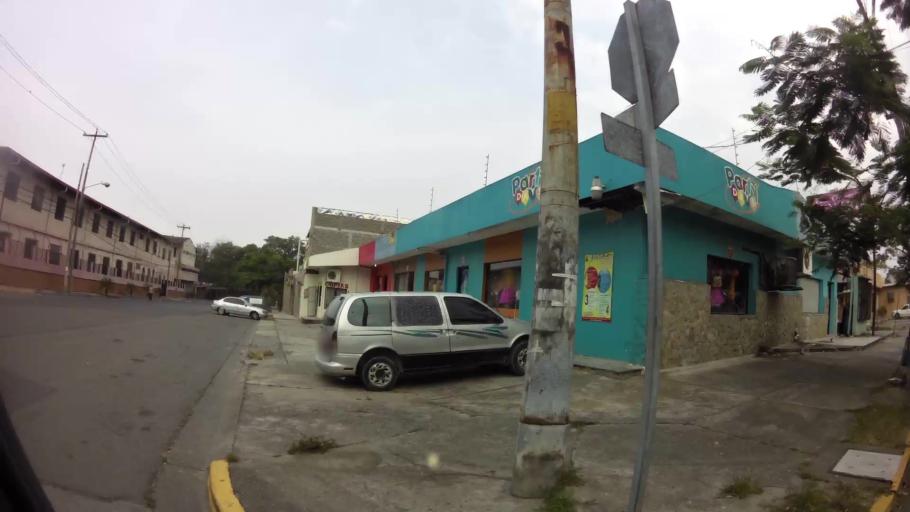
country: HN
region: Cortes
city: San Pedro Sula
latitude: 15.5084
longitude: -88.0320
